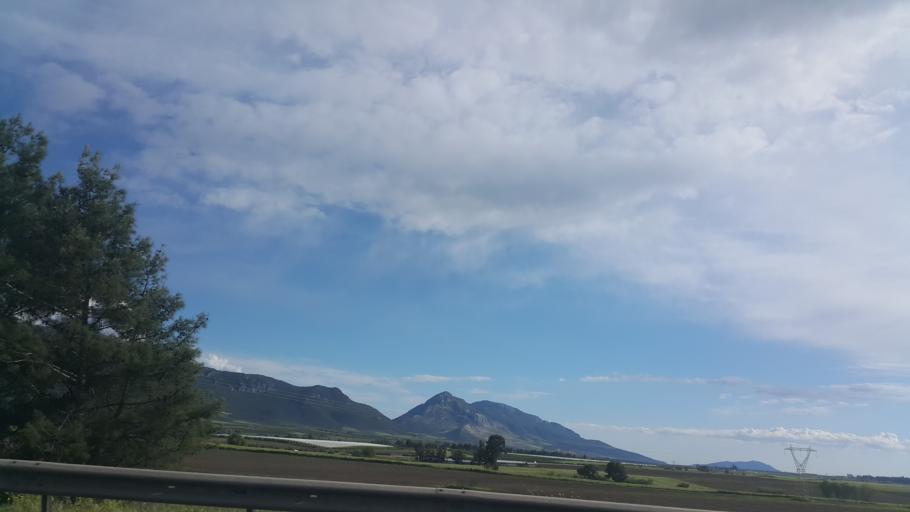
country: TR
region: Adana
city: Yakapinar
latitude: 37.0071
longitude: 35.6869
